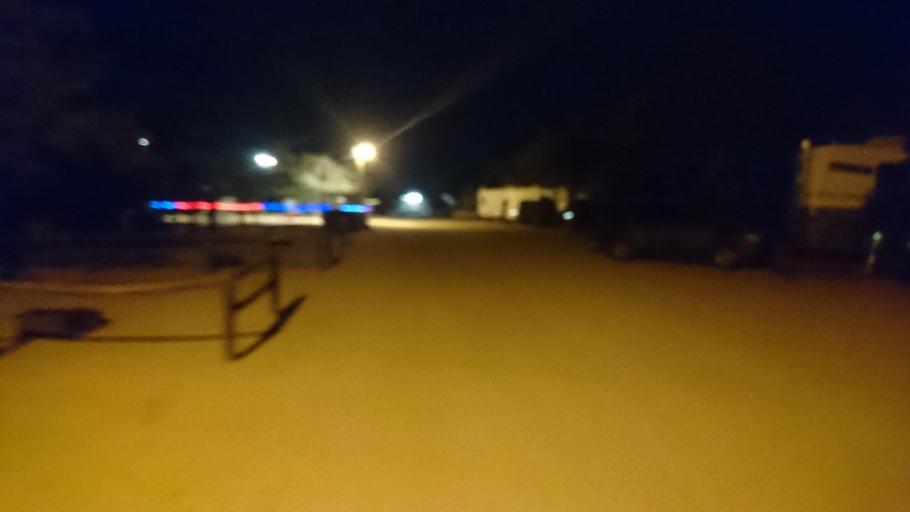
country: US
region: Arizona
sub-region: Mohave County
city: New Kingman-Butler
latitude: 35.2353
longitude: -114.0178
